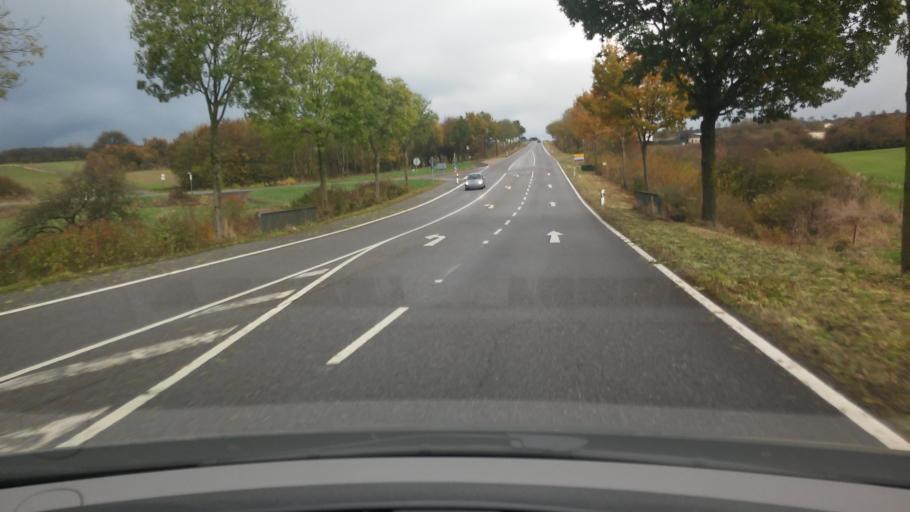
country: FR
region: Lorraine
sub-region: Departement de la Moselle
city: Merten
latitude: 49.2975
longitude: 6.6684
